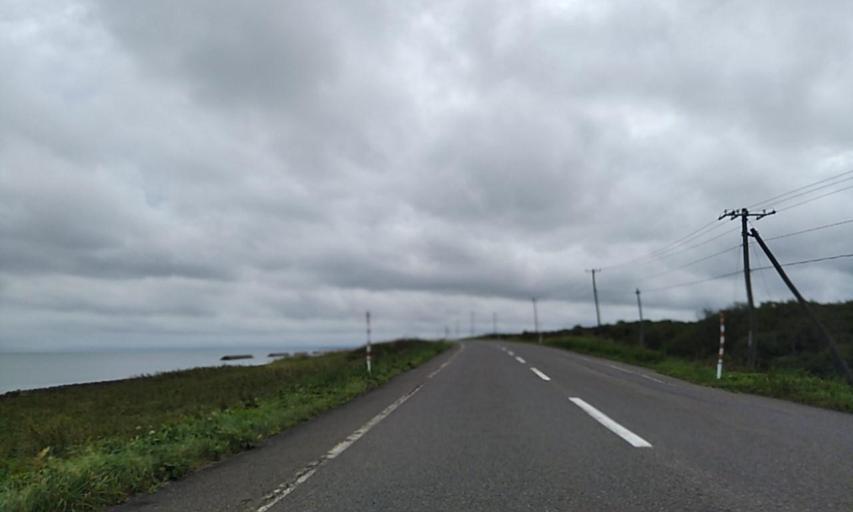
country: JP
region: Hokkaido
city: Shibetsu
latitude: 43.4353
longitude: 145.2624
